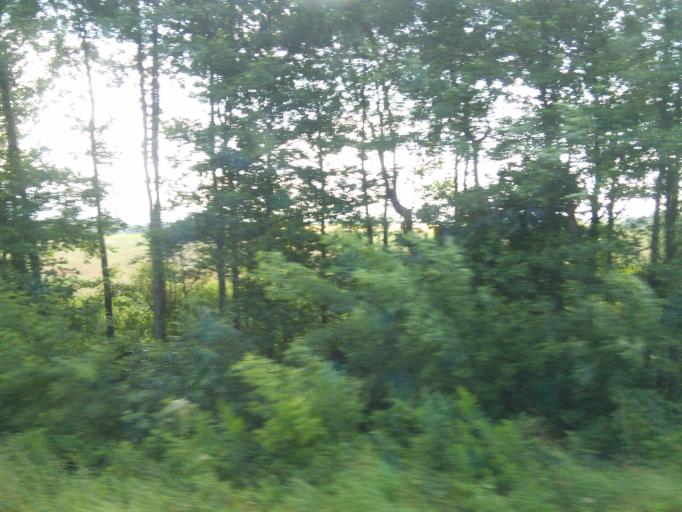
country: BY
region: Minsk
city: Maladzyechna
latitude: 54.2867
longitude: 26.9404
